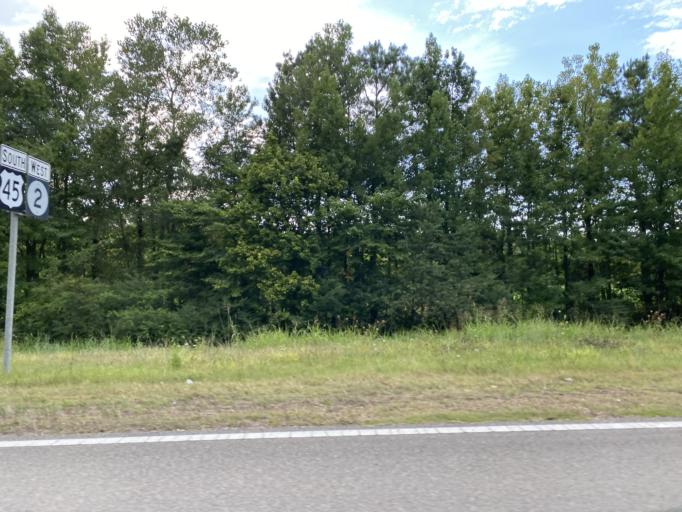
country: US
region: Mississippi
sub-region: Alcorn County
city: Corinth
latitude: 34.9775
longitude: -88.5248
